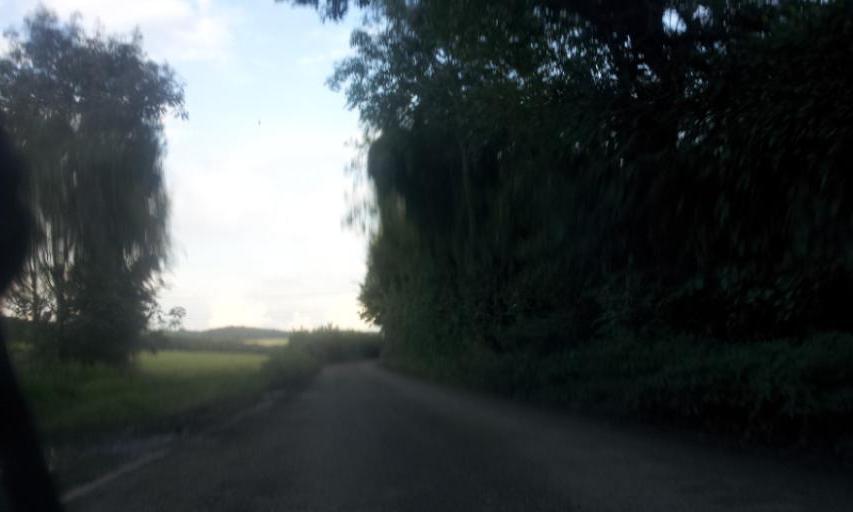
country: GB
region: England
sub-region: Kent
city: Meopham
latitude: 51.3749
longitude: 0.4021
